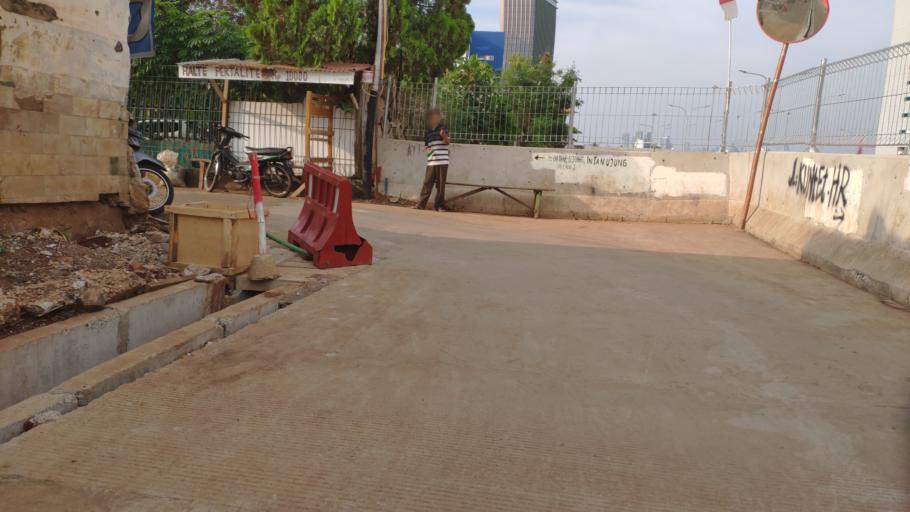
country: ID
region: West Java
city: Pamulang
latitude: -6.2955
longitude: 106.8045
